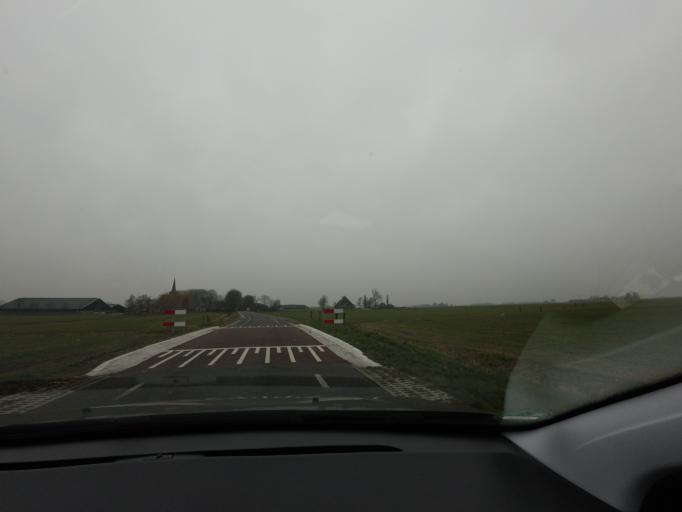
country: NL
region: Friesland
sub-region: Sudwest Fryslan
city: Bolsward
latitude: 53.1077
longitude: 5.5409
